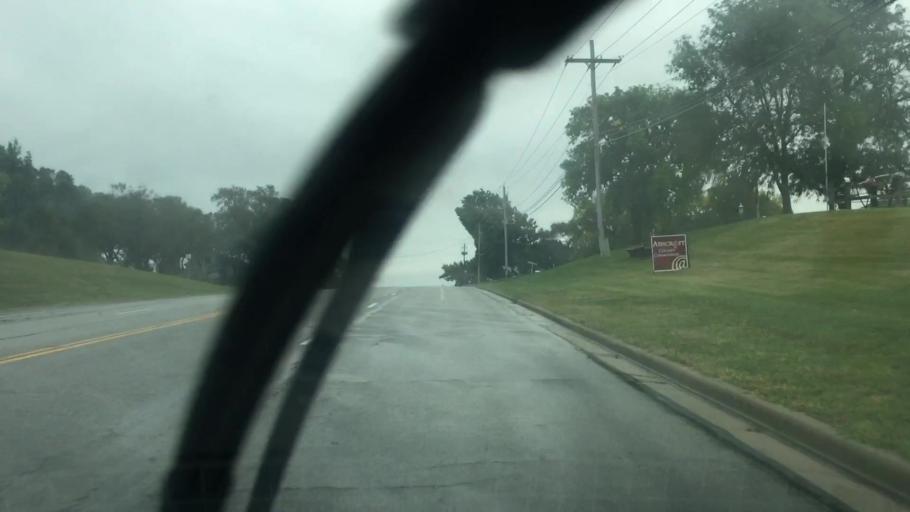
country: US
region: Kansas
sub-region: Johnson County
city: Lenexa
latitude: 38.9709
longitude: -94.8062
